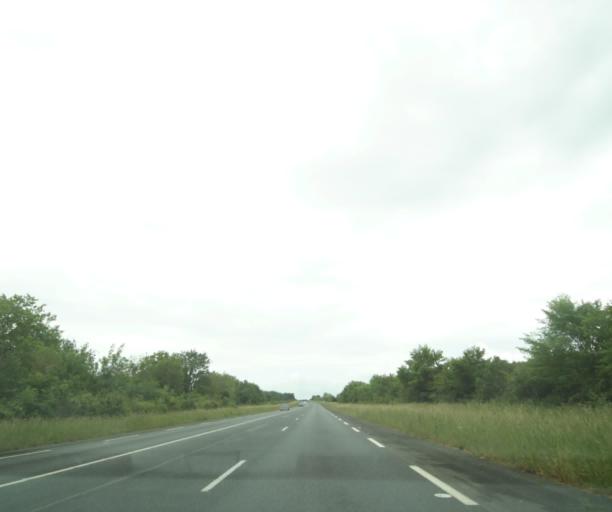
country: FR
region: Poitou-Charentes
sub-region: Departement des Deux-Sevres
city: Saint-Varent
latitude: 46.8515
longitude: -0.2087
